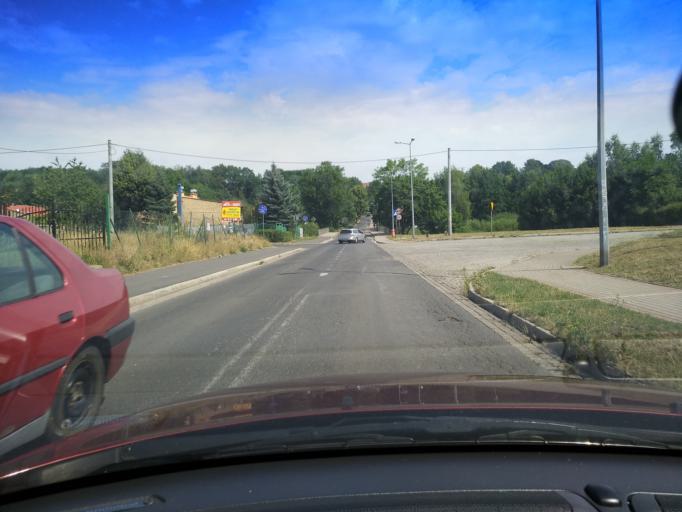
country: PL
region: Lower Silesian Voivodeship
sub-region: Powiat zgorzelecki
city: Zgorzelec
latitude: 51.1340
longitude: 15.0060
